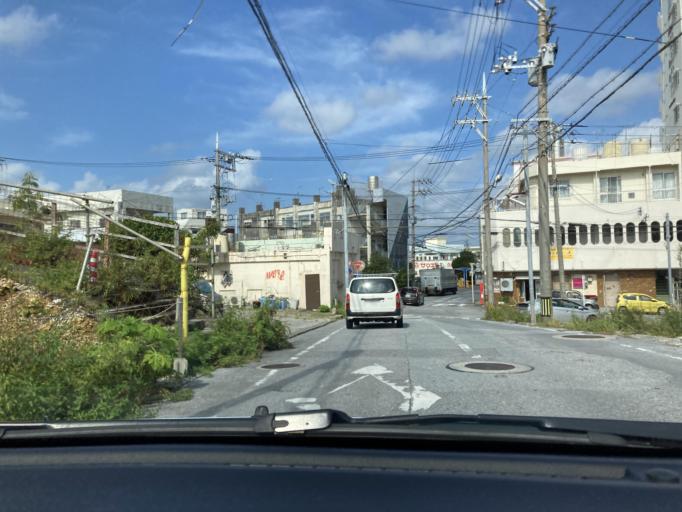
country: JP
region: Okinawa
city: Chatan
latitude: 26.2907
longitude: 127.7768
